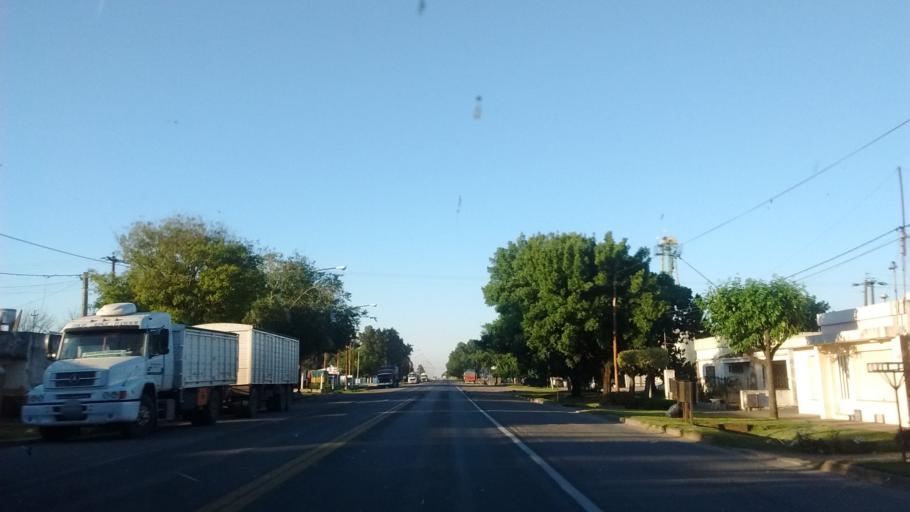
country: AR
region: Santa Fe
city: Firmat
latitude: -33.2499
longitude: -61.3630
